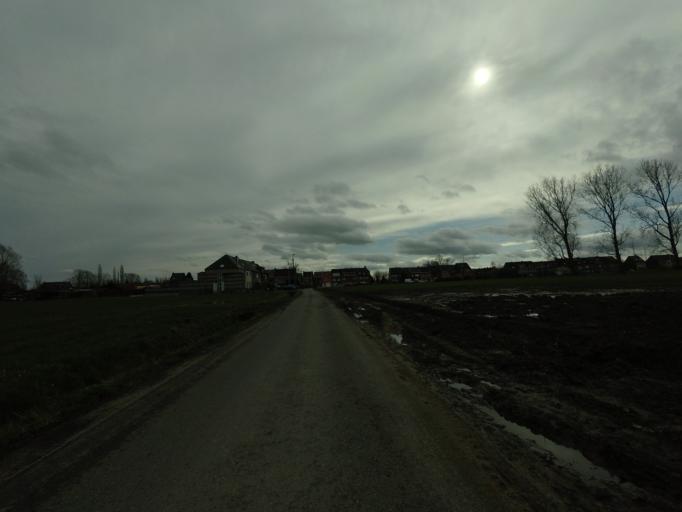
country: BE
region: Flanders
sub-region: Provincie Antwerpen
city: Schelle
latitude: 51.1273
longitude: 4.3563
